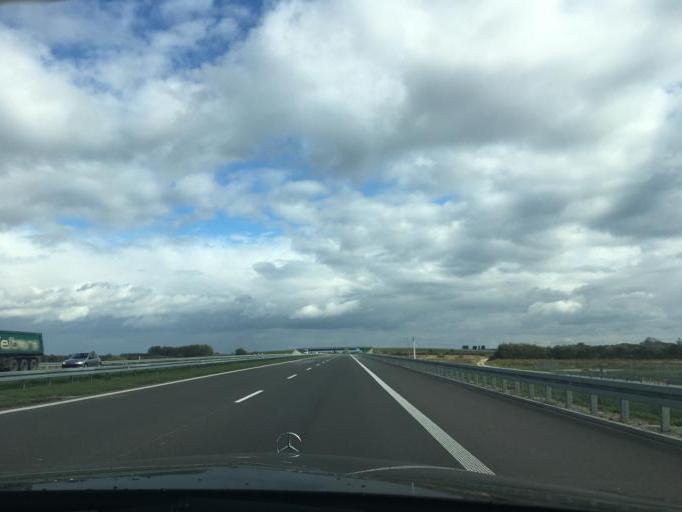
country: PL
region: Subcarpathian Voivodeship
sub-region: Powiat rzeszowski
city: Wolka Podlesna
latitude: 50.0933
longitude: 22.0907
